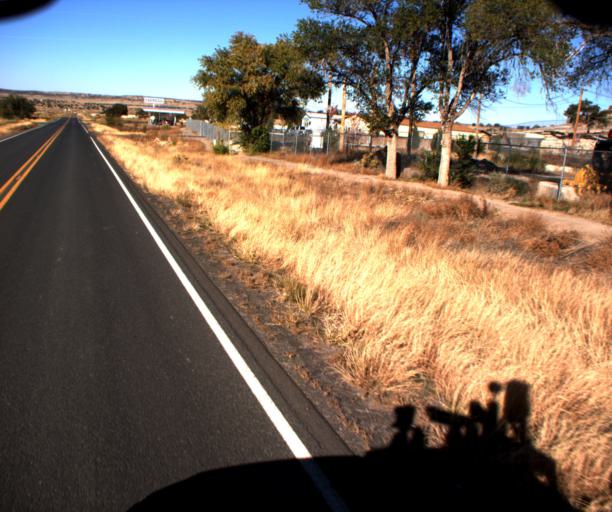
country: US
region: Arizona
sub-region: Apache County
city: Ganado
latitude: 35.7468
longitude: -109.8571
